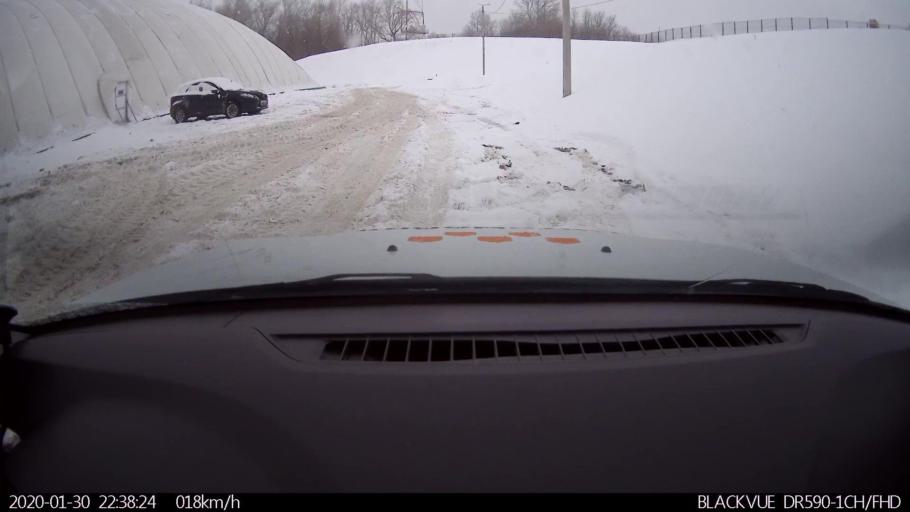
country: RU
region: Nizjnij Novgorod
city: Nizhniy Novgorod
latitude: 56.2926
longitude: 43.9753
